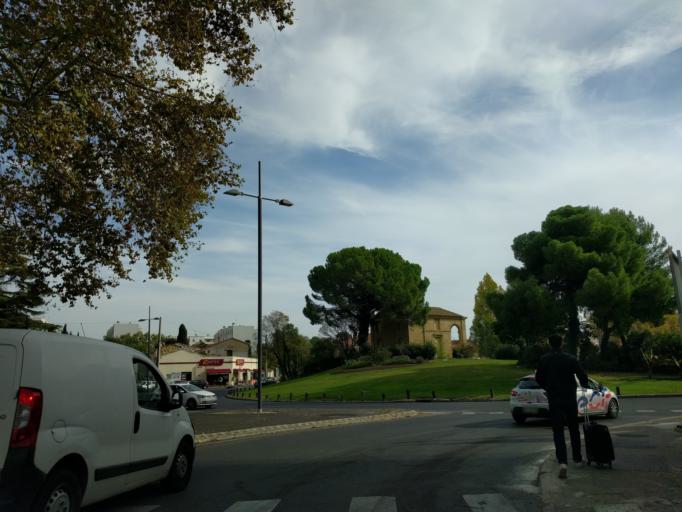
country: FR
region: Languedoc-Roussillon
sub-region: Departement de l'Herault
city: Montpellier
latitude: 43.6061
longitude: 3.8982
